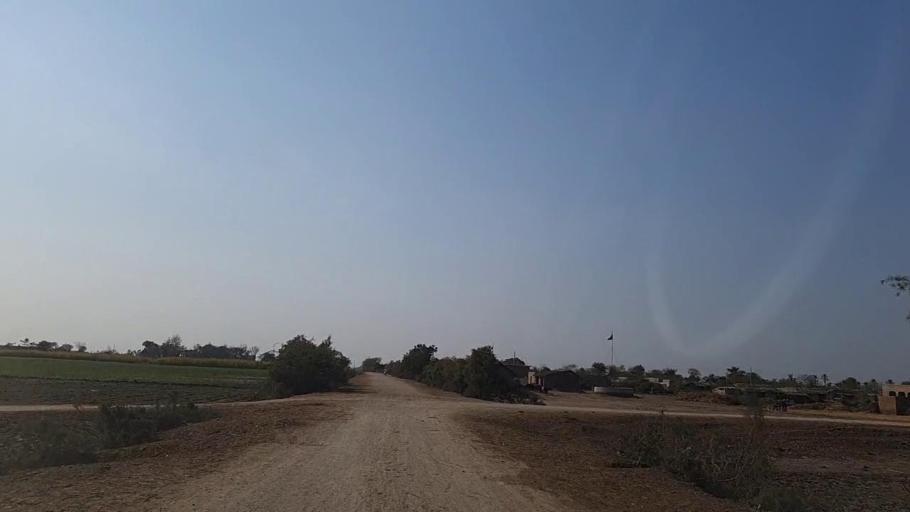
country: PK
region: Sindh
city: Daur
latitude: 26.4368
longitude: 68.2631
